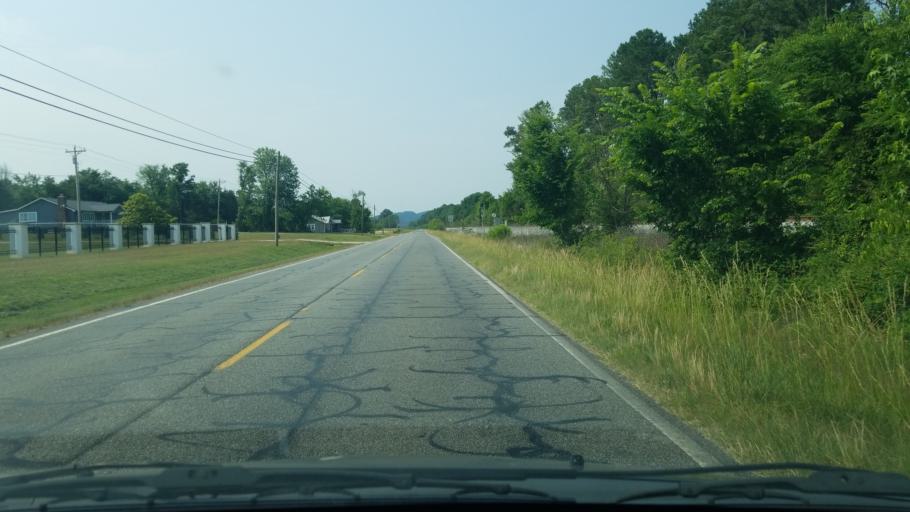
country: US
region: Georgia
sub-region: Catoosa County
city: Ringgold
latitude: 34.9516
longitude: -85.1041
